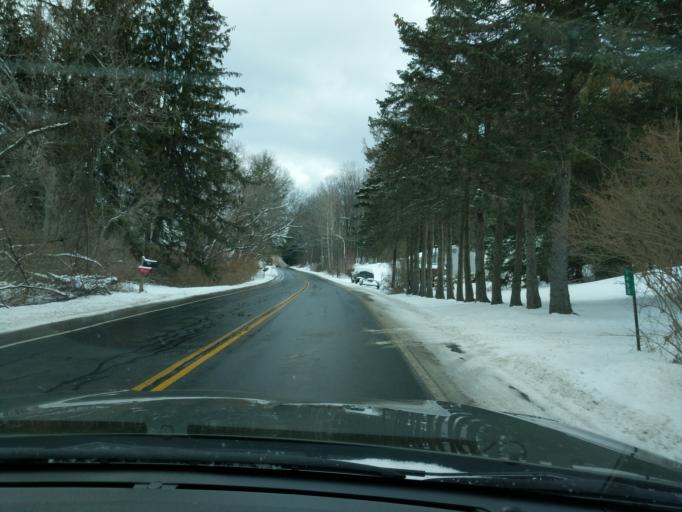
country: US
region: New York
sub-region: Tompkins County
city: Northeast Ithaca
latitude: 42.4271
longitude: -76.4102
